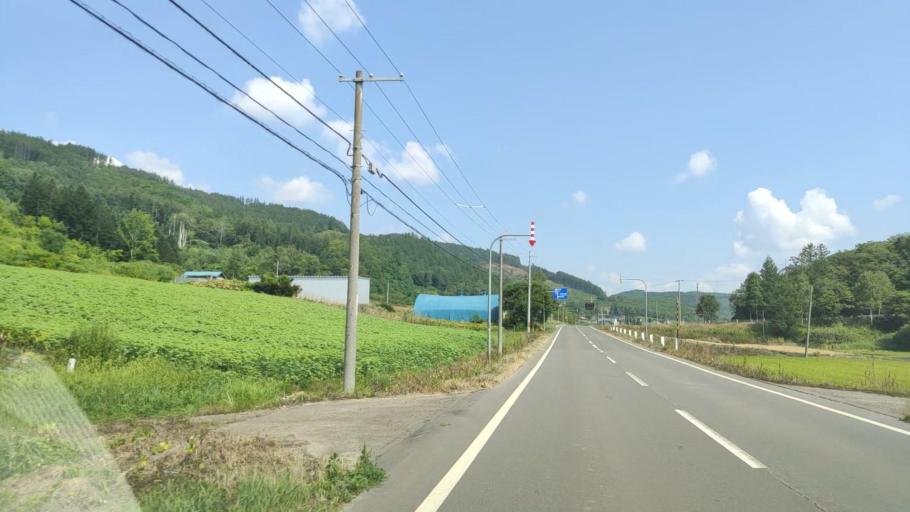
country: JP
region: Hokkaido
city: Shimo-furano
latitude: 43.4332
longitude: 142.4096
